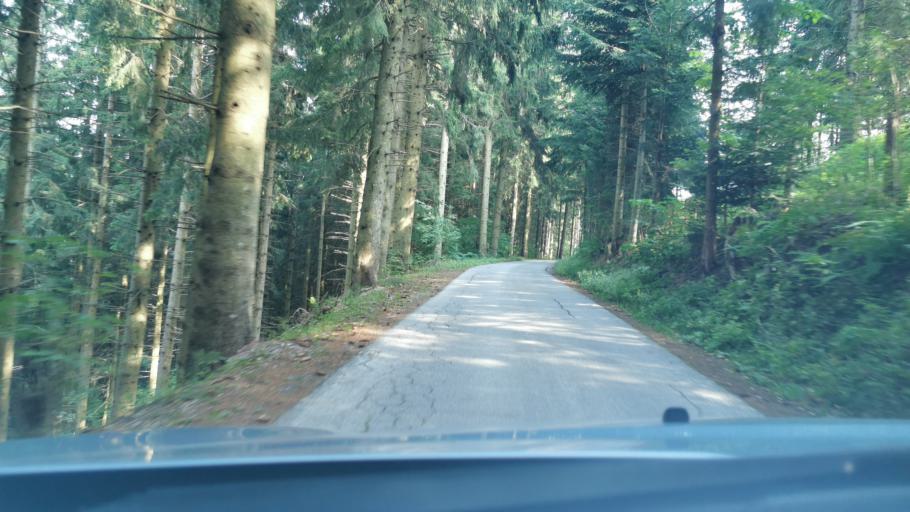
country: AT
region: Styria
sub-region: Politischer Bezirk Weiz
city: Fischbach
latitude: 47.3986
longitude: 15.6432
